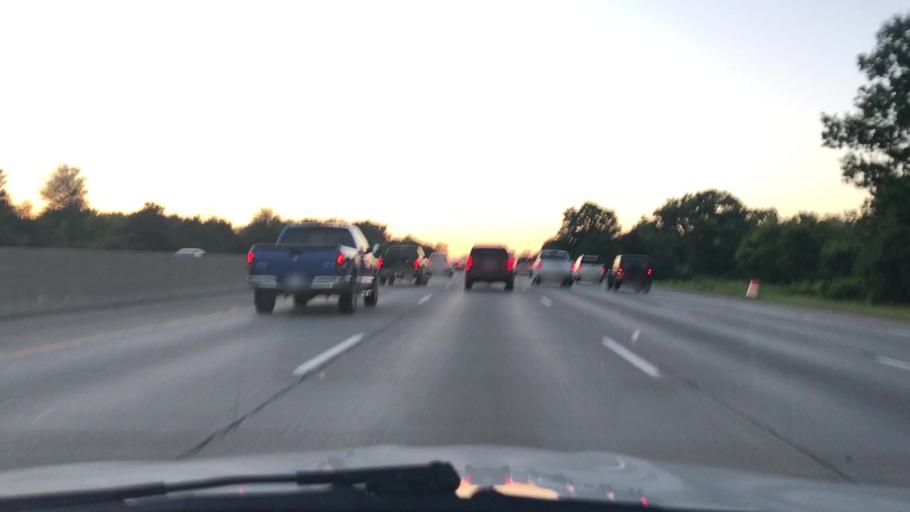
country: US
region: Michigan
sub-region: Oakland County
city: Farmington Hills
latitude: 42.4953
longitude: -83.3722
